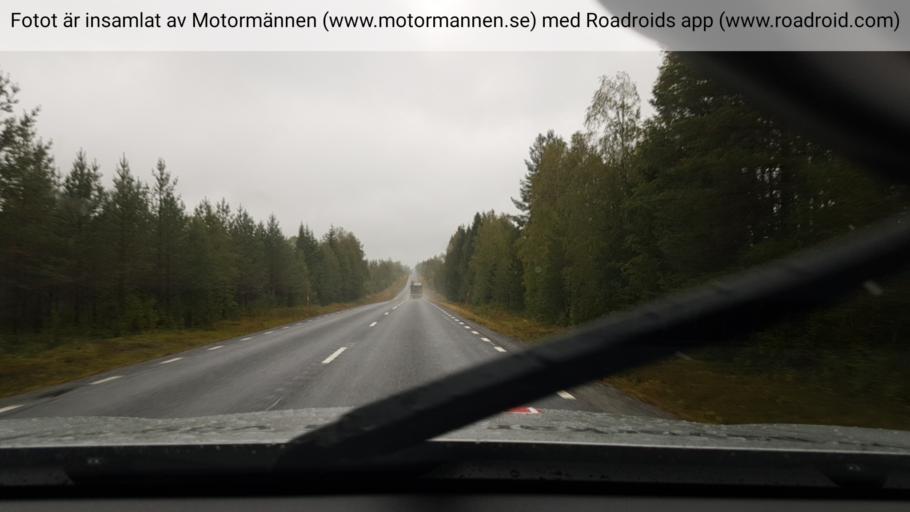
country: SE
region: Vaesterbotten
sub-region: Bjurholms Kommun
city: Bjurholm
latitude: 63.9433
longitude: 18.9202
